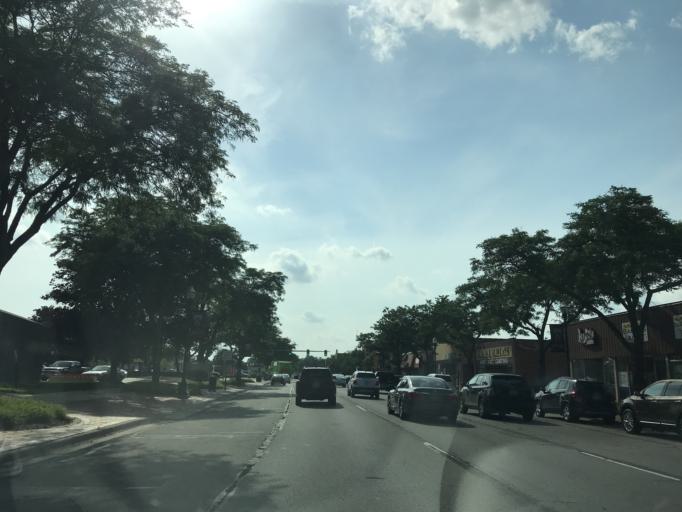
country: US
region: Michigan
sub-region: Wayne County
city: Wayne
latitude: 42.2821
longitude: -83.3823
